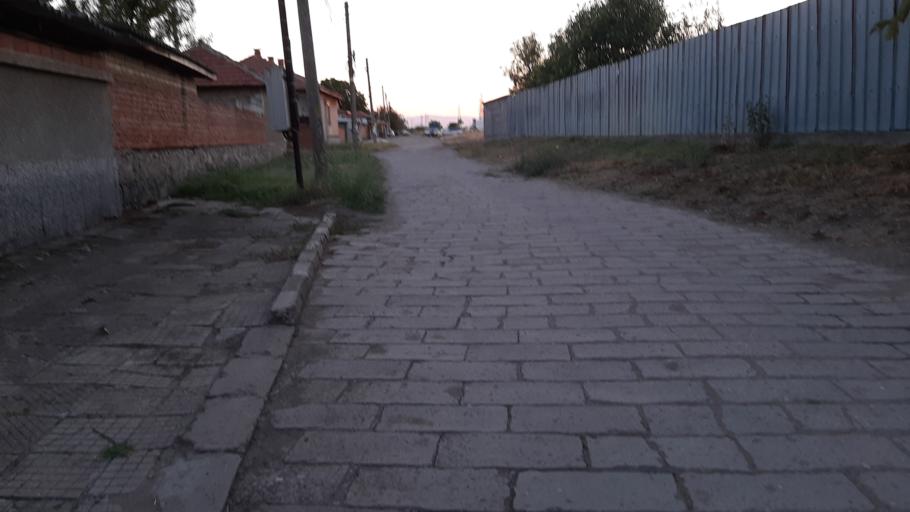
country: BG
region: Stara Zagora
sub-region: Obshtina Chirpan
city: Chirpan
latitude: 42.1073
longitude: 25.2185
